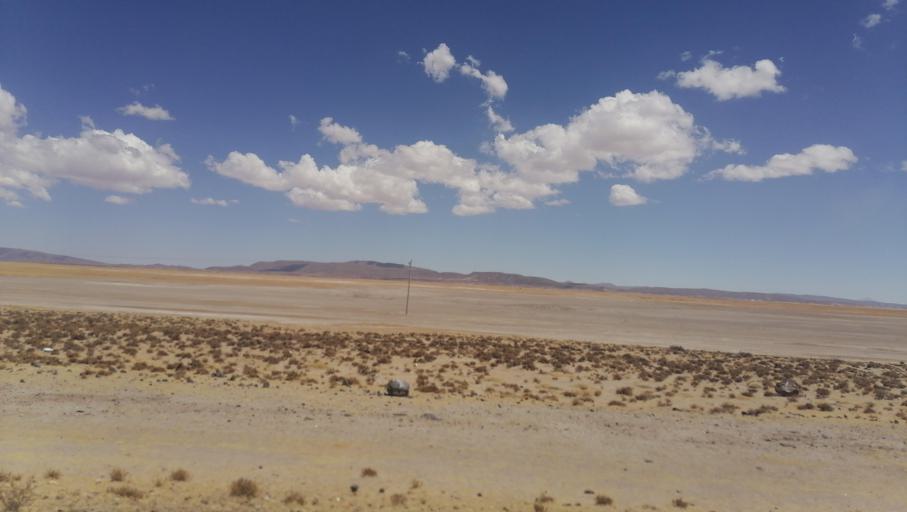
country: BO
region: Oruro
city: Challapata
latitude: -19.2157
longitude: -67.0169
